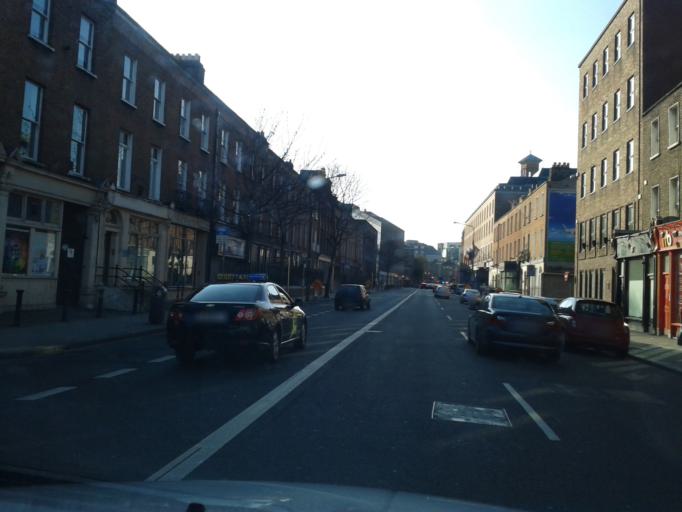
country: IE
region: Leinster
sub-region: Dublin City
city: Dublin
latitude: 53.3448
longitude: -6.2525
